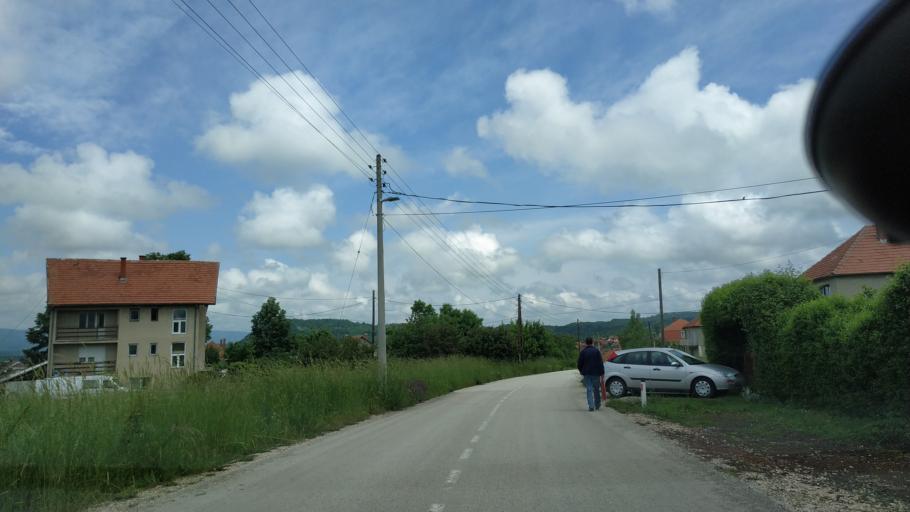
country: RS
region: Central Serbia
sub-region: Zajecarski Okrug
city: Boljevac
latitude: 43.8252
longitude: 21.9570
